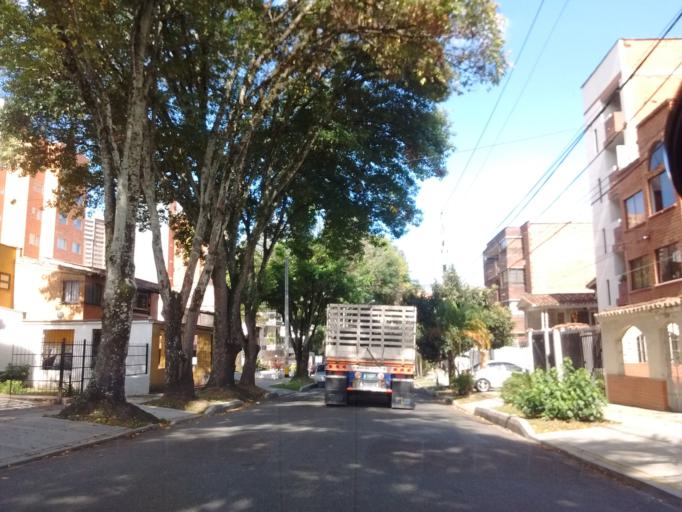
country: CO
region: Antioquia
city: Medellin
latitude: 6.2691
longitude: -75.5942
